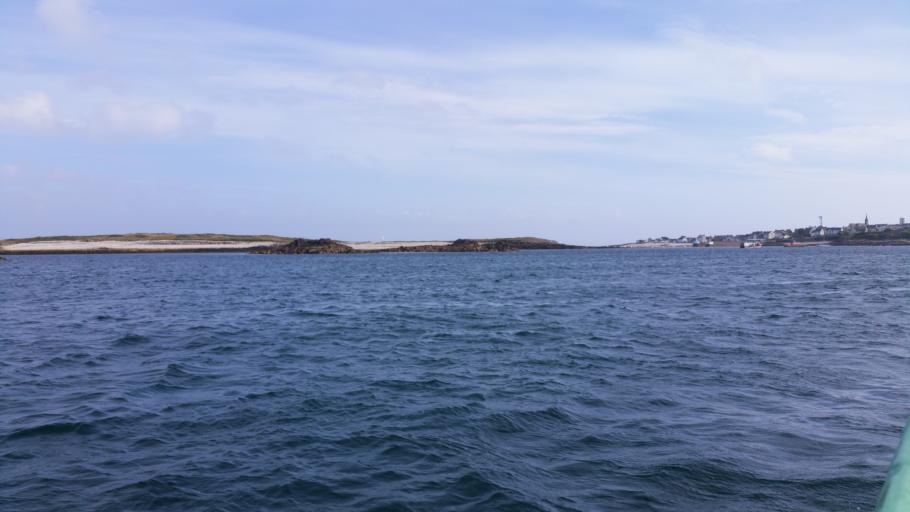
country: FR
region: Brittany
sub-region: Departement du Finistere
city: Le Conquet
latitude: 48.4064
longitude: -4.9529
